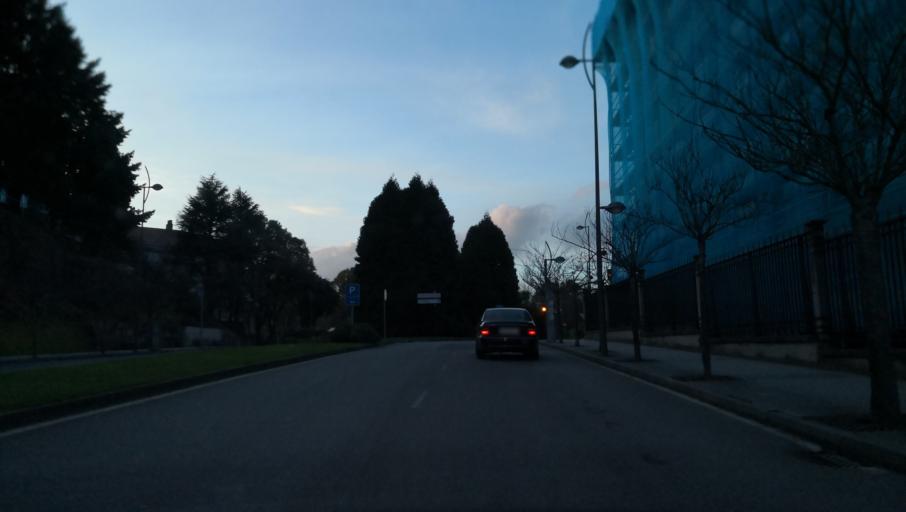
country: ES
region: Galicia
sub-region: Provincia da Coruna
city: Santiago de Compostela
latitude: 42.8881
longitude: -8.5351
